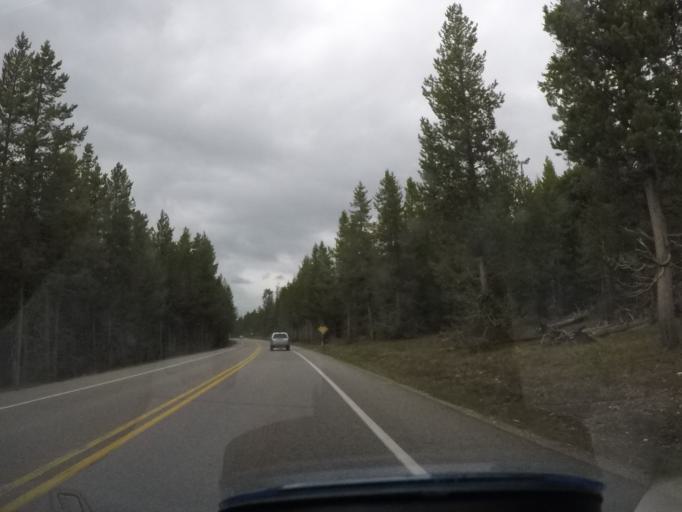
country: US
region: Wyoming
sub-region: Teton County
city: Moose Wilson Road
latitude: 43.9084
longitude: -110.6268
